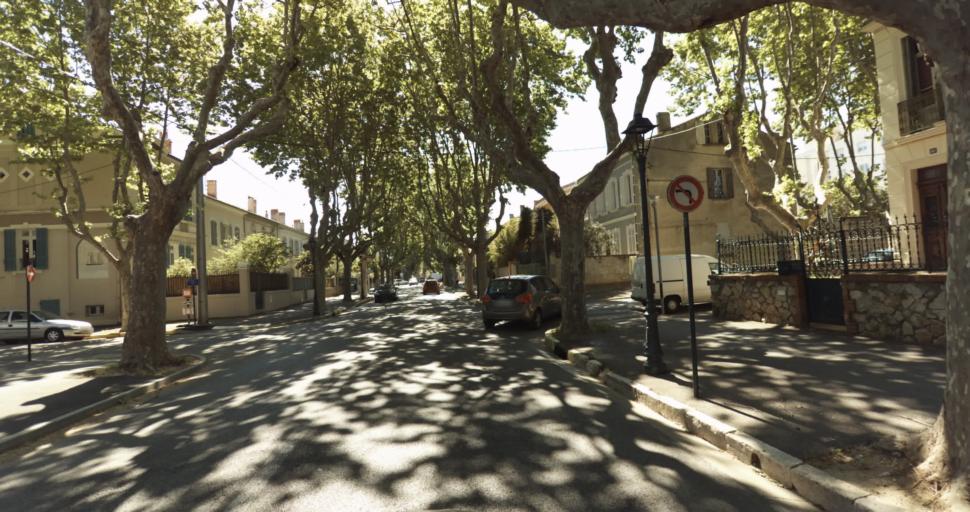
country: FR
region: Provence-Alpes-Cote d'Azur
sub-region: Departement du Var
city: La Seyne-sur-Mer
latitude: 43.1034
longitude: 5.8730
